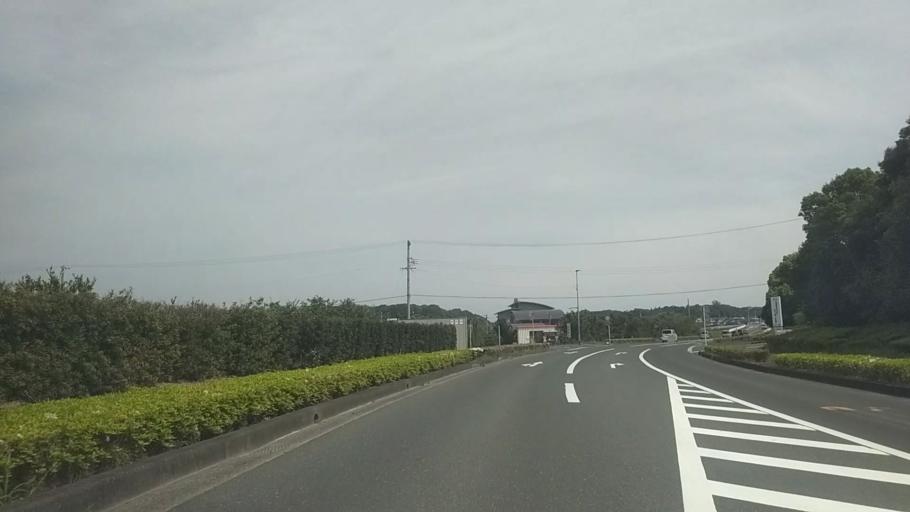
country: JP
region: Shizuoka
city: Hamamatsu
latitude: 34.7976
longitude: 137.6409
